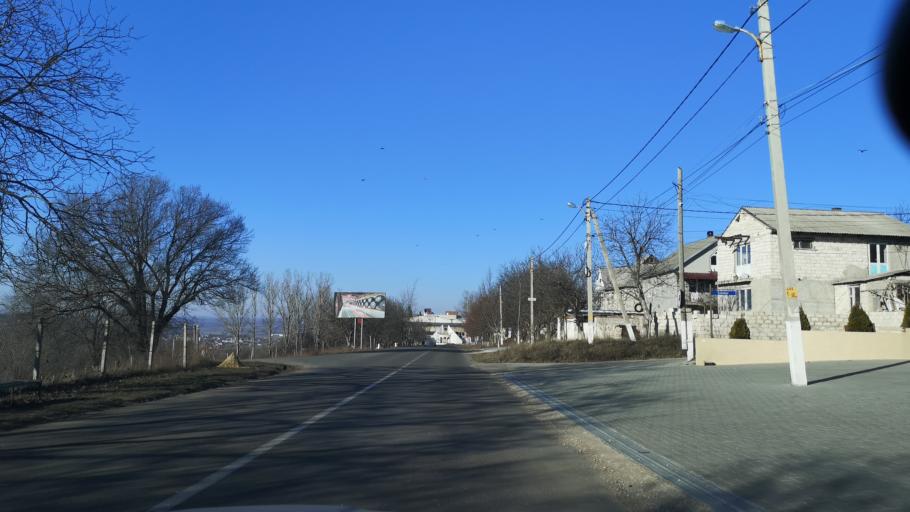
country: MD
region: Chisinau
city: Cricova
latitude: 47.1349
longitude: 28.8569
